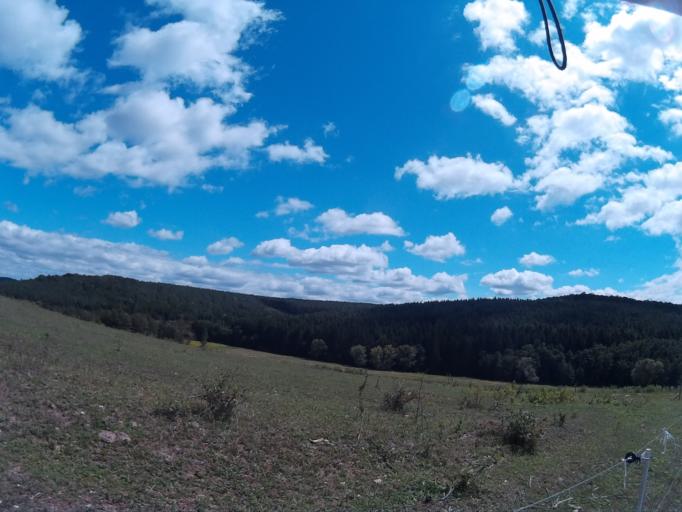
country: HU
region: Zala
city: Zalalovo
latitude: 46.8261
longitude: 16.5977
